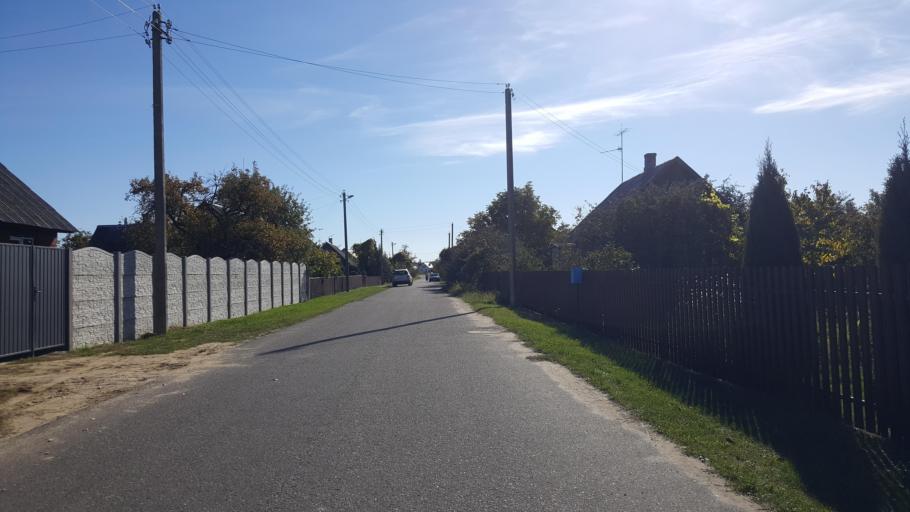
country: BY
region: Brest
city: Kamyanyets
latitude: 52.3984
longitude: 23.8154
